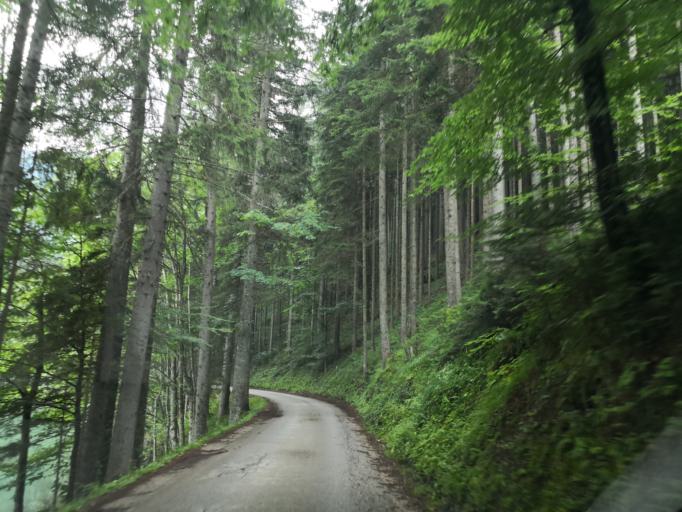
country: SI
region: Jezersko
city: Zgornje Jezersko
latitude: 46.4026
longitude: 14.5148
